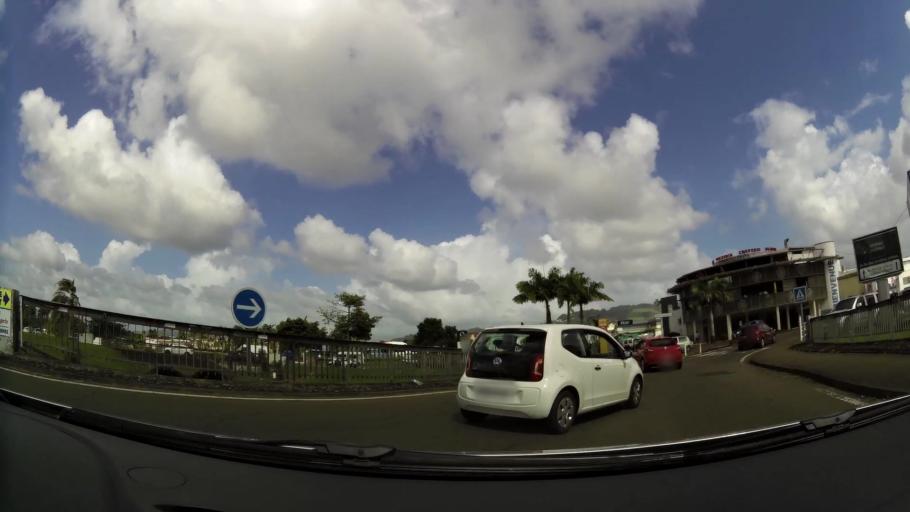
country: MQ
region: Martinique
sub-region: Martinique
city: Le Lamentin
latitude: 14.6141
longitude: -60.9943
